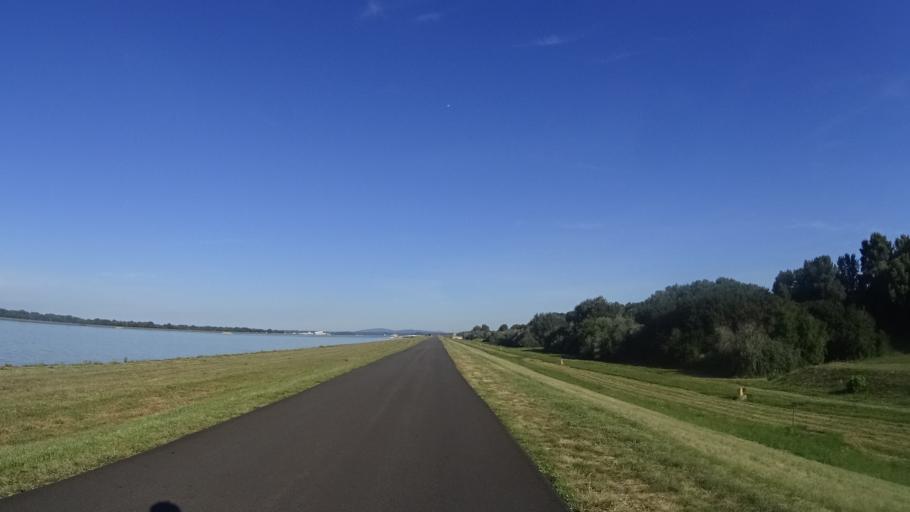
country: SK
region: Trnavsky
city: Samorin
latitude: 48.0287
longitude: 17.2589
